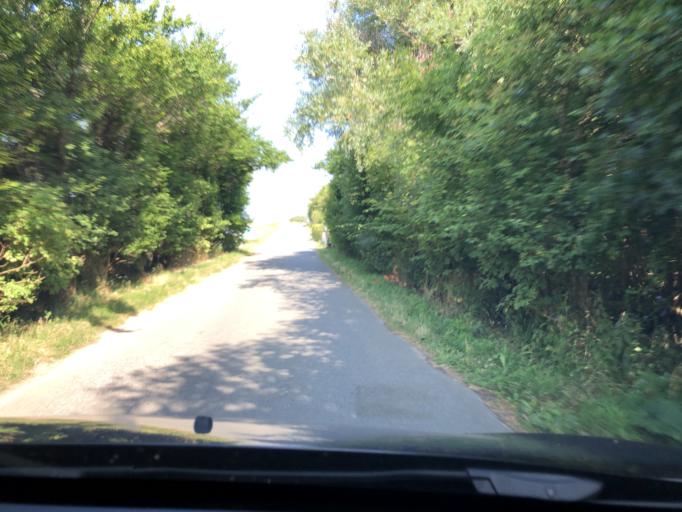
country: DK
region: South Denmark
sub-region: Faaborg-Midtfyn Kommune
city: Faaborg
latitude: 54.9489
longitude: 10.2333
